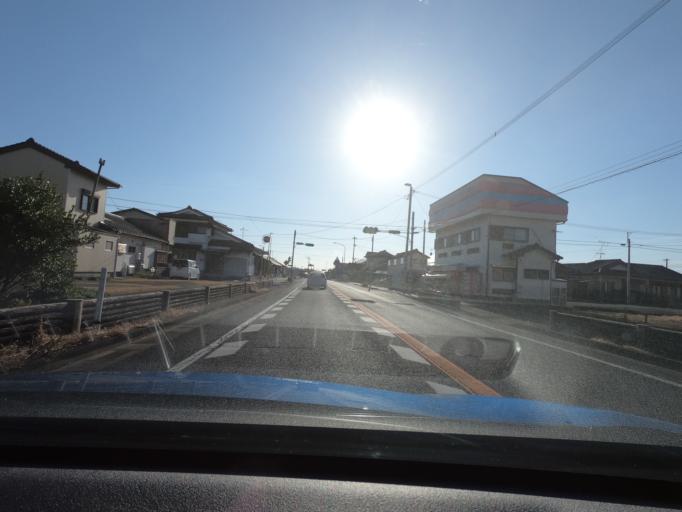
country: JP
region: Kagoshima
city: Izumi
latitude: 32.1293
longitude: 130.3449
